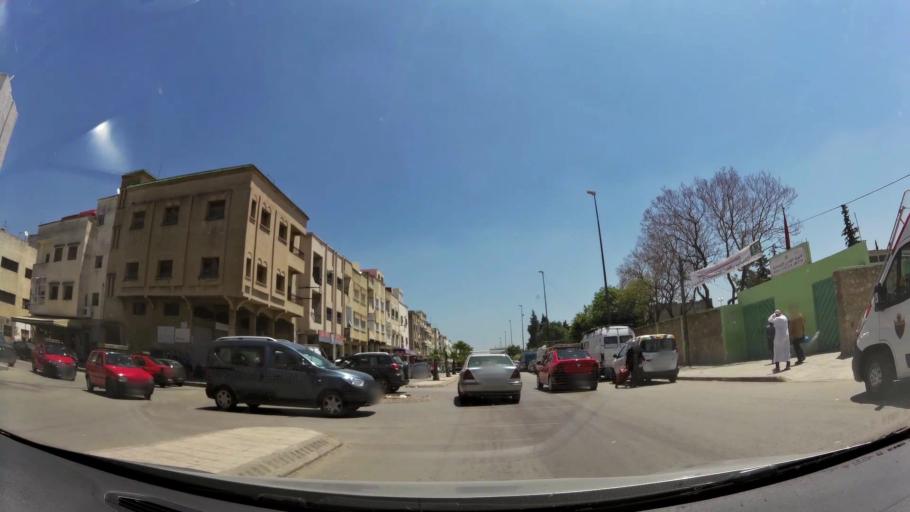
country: MA
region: Fes-Boulemane
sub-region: Fes
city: Fes
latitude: 34.0216
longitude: -5.0096
